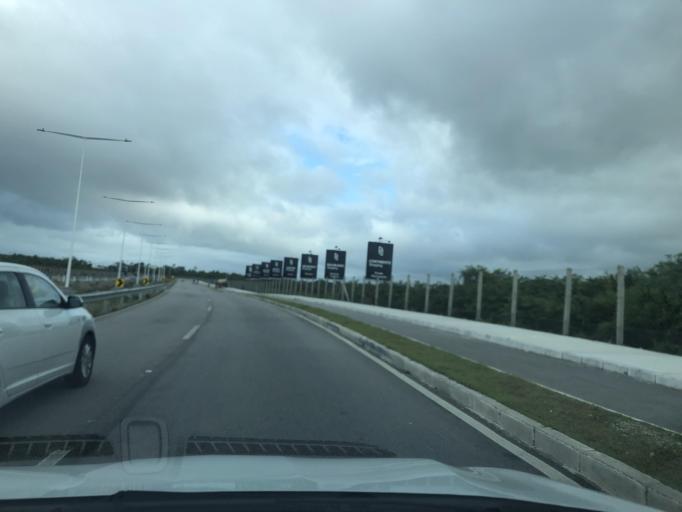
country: BR
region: Santa Catarina
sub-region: Florianopolis
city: Carianos
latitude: -27.6760
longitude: -48.5271
